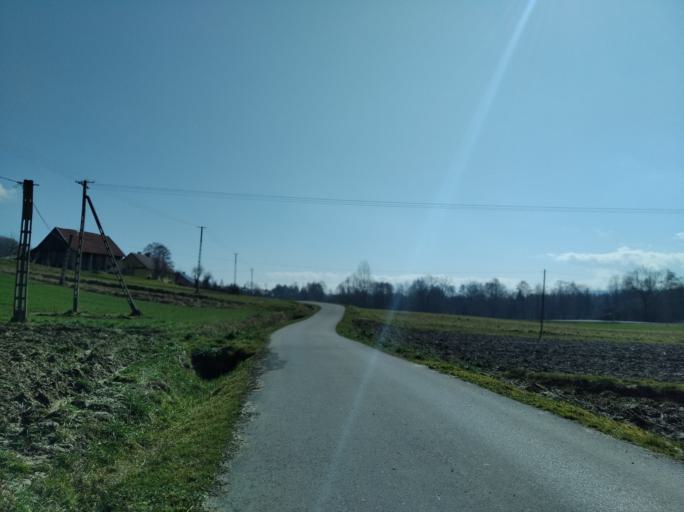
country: PL
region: Subcarpathian Voivodeship
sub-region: Powiat strzyzowski
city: Wysoka Strzyzowska
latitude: 49.8453
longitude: 21.7356
